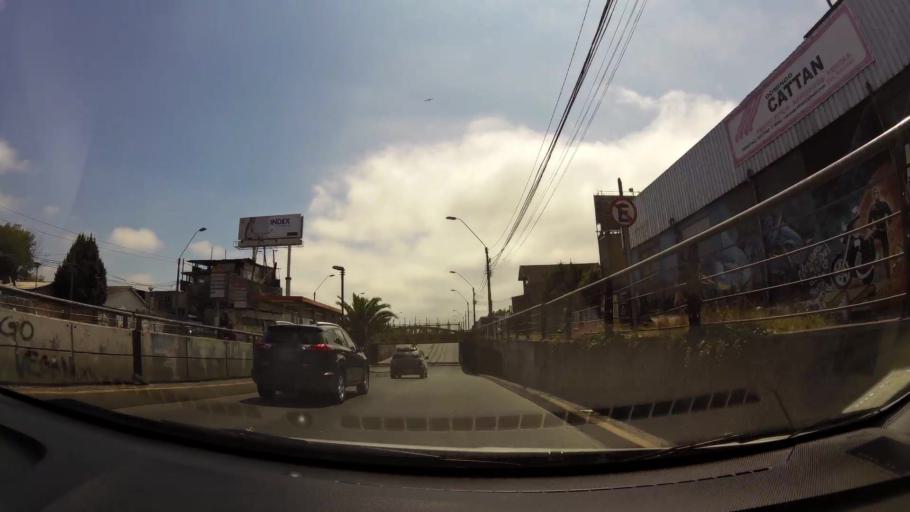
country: CL
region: Biobio
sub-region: Provincia de Concepcion
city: Concepcion
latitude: -36.8127
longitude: -73.0489
